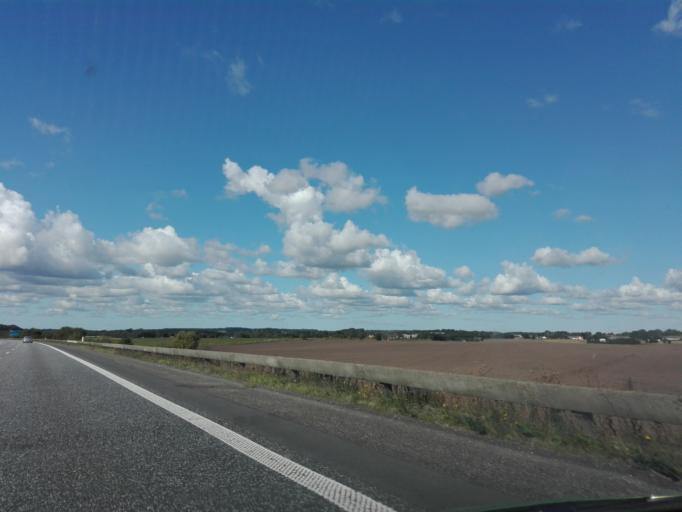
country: DK
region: Central Jutland
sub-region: Randers Kommune
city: Spentrup
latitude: 56.5333
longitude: 9.9268
